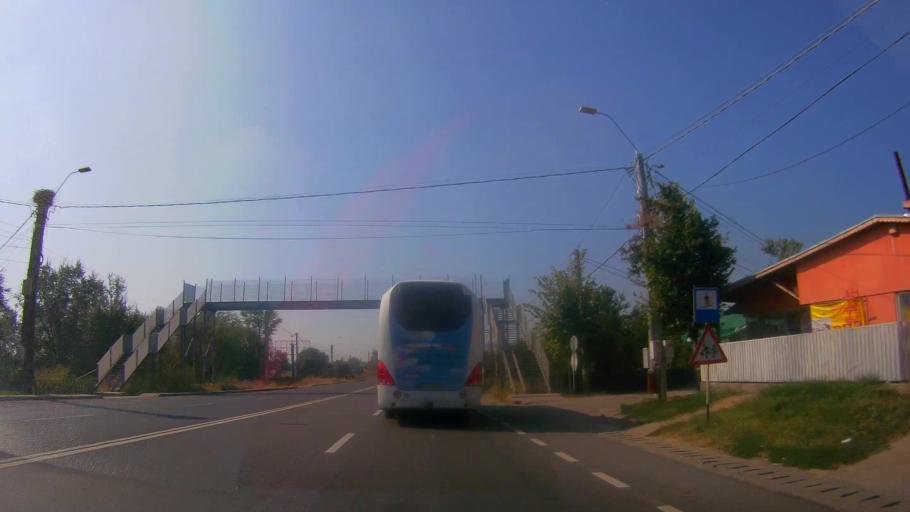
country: RO
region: Giurgiu
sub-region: Comuna Daia
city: Daia
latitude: 43.9945
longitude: 25.9923
